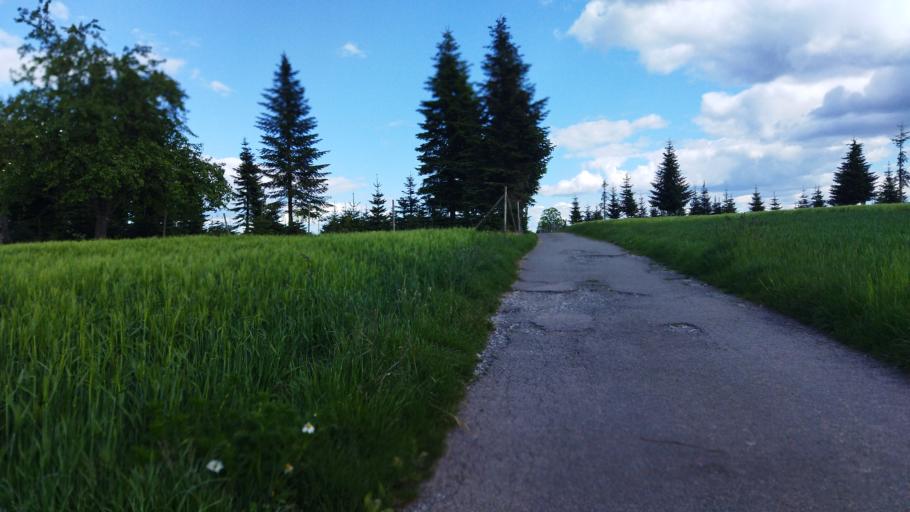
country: DE
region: Baden-Wuerttemberg
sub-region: Karlsruhe Region
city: Zwingenberg
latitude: 49.4506
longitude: 9.0628
